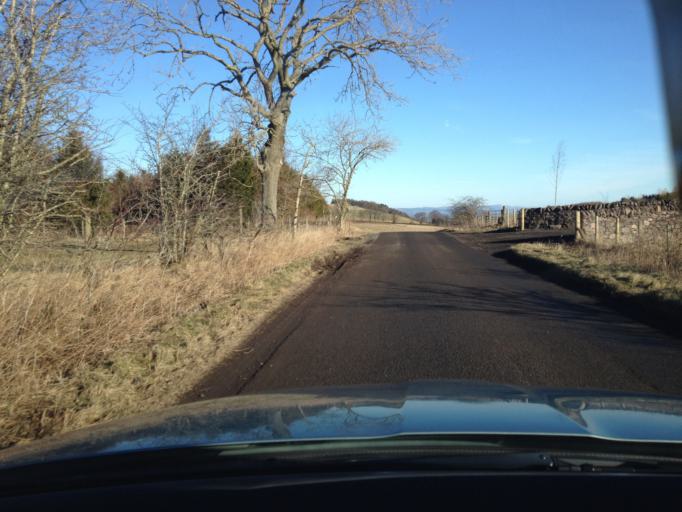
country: GB
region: Scotland
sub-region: Perth and Kinross
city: Bridge of Earn
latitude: 56.2980
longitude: -3.3965
